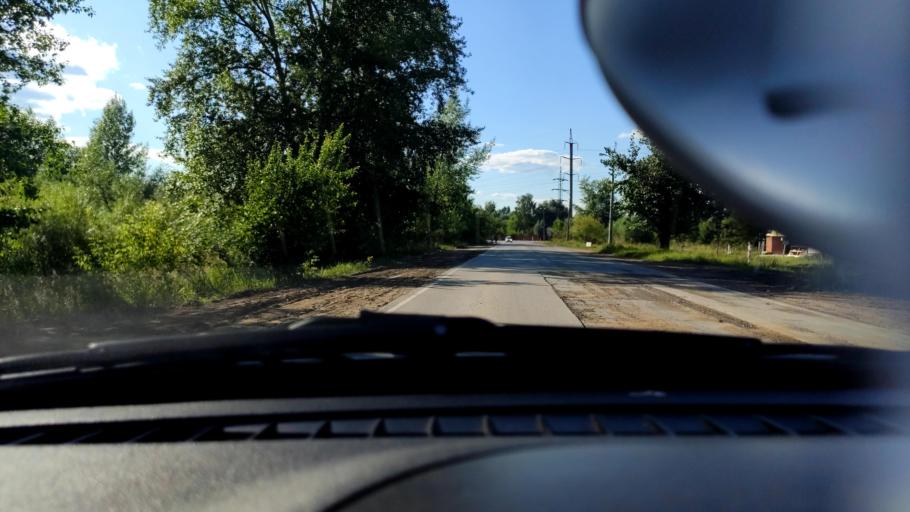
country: RU
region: Perm
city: Krasnokamsk
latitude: 58.0730
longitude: 55.7988
